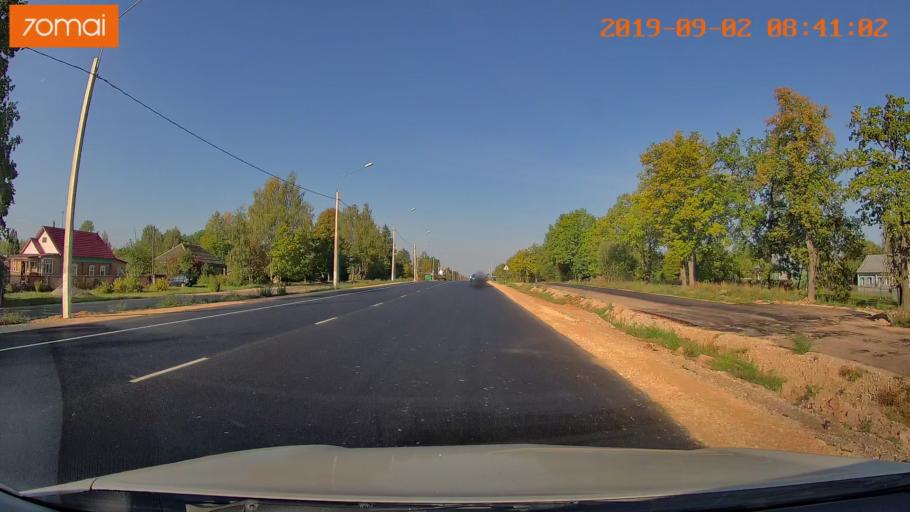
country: RU
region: Kaluga
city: Kudinovo
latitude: 54.9736
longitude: 36.1198
